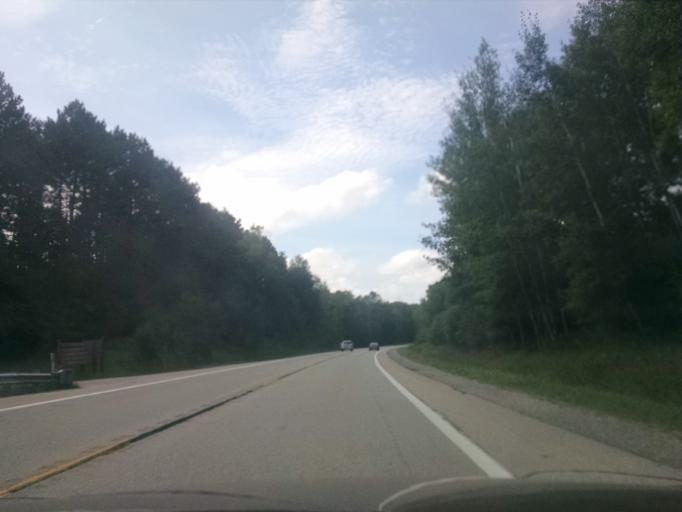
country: US
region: Michigan
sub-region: Clare County
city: Clare
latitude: 43.8710
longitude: -84.9353
